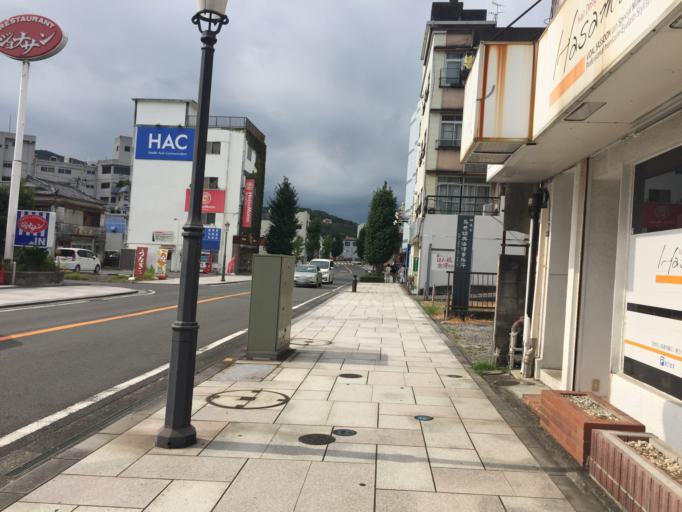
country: JP
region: Shizuoka
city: Ito
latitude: 34.9698
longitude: 139.0973
